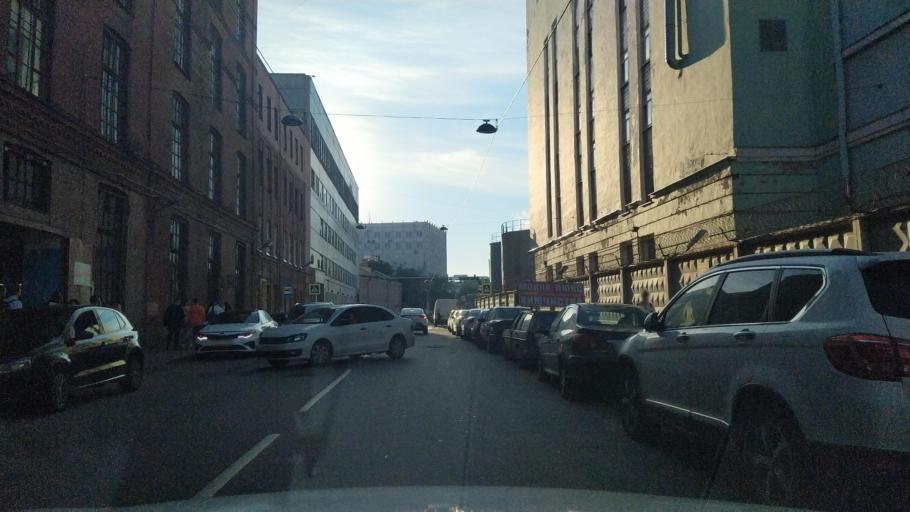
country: RU
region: St.-Petersburg
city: Vasyl'evsky Ostrov
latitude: 59.9237
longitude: 30.2461
